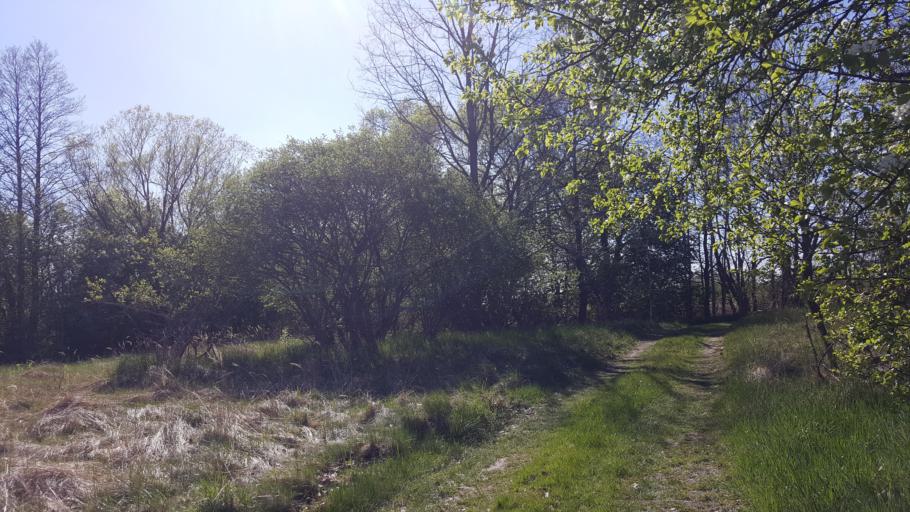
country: BY
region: Brest
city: Kamyanyets
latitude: 52.4364
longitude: 23.8746
